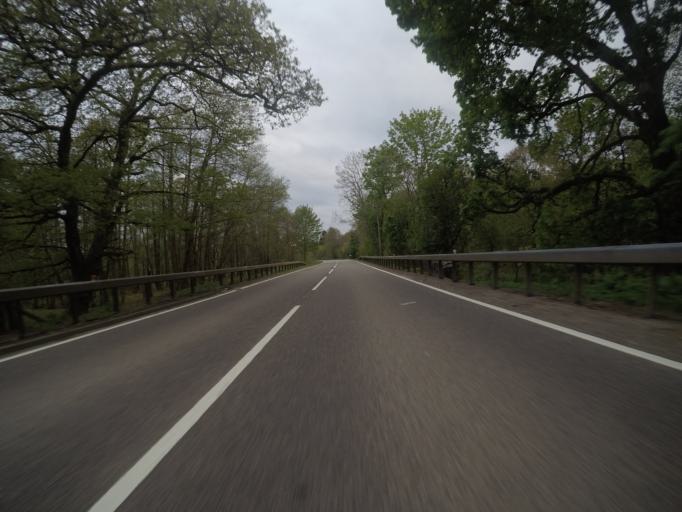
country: GB
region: Scotland
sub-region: Highland
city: Spean Bridge
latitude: 56.8954
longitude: -4.9024
